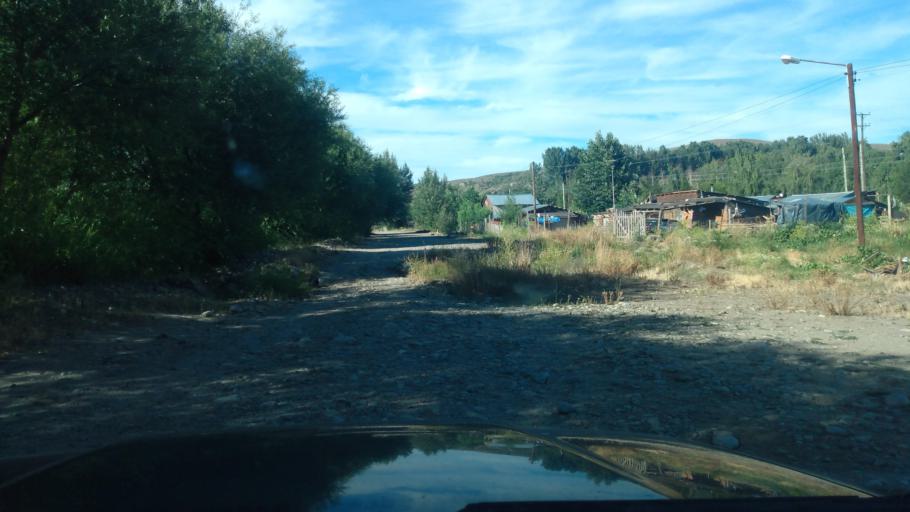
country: AR
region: Neuquen
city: Junin de los Andes
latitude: -39.9605
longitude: -71.0783
